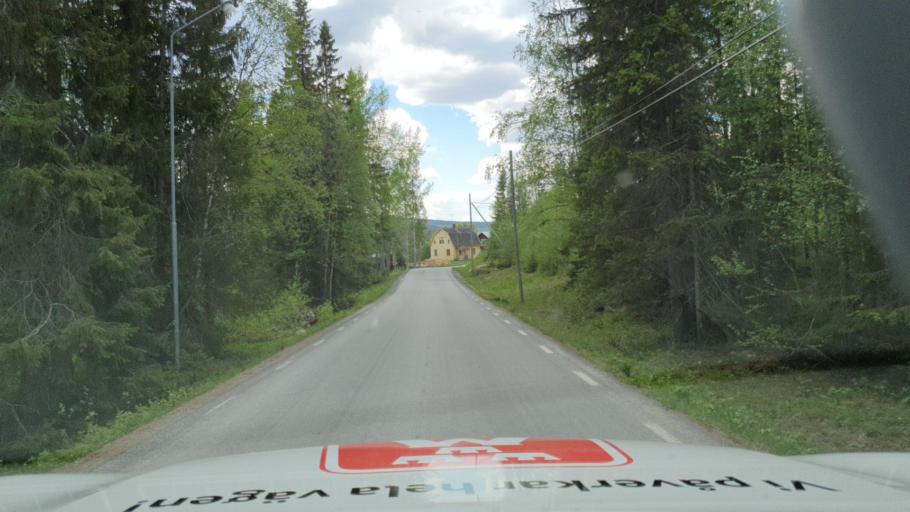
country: SE
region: Jaemtland
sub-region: Krokoms Kommun
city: Valla
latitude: 63.9702
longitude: 14.1449
